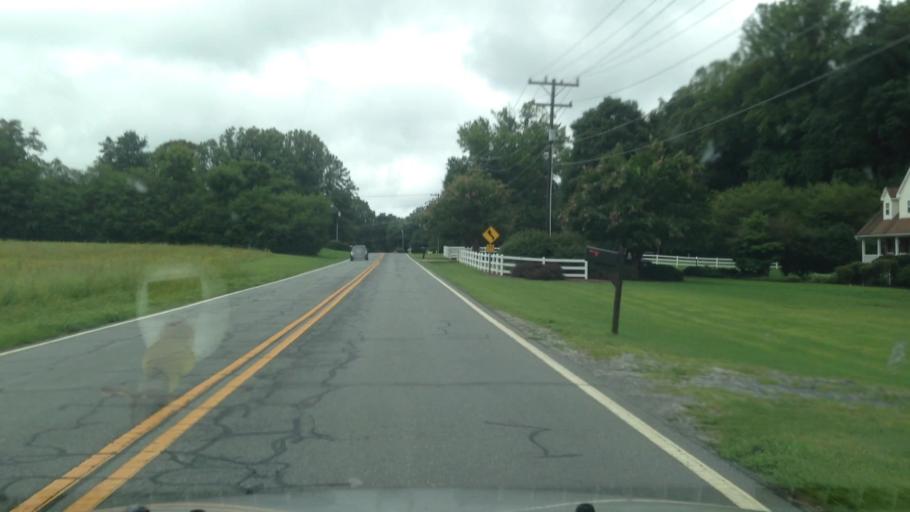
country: US
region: North Carolina
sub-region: Forsyth County
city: Kernersville
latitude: 36.1890
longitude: -80.0590
